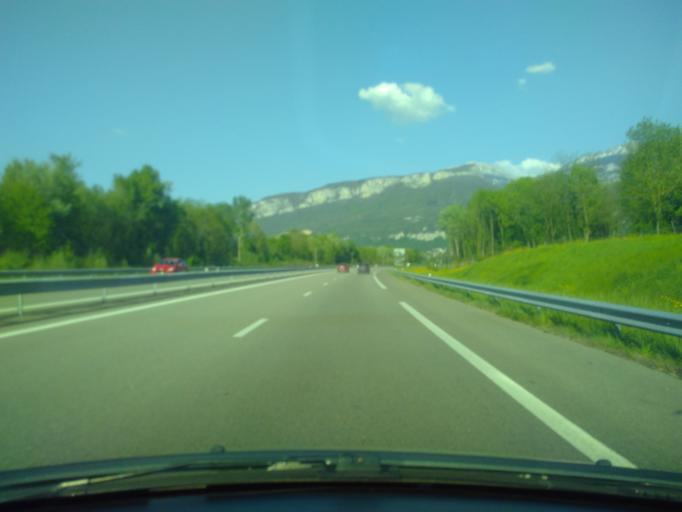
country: FR
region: Rhone-Alpes
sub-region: Departement de l'Isere
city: Veurey-Voroize
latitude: 45.3021
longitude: 5.5884
